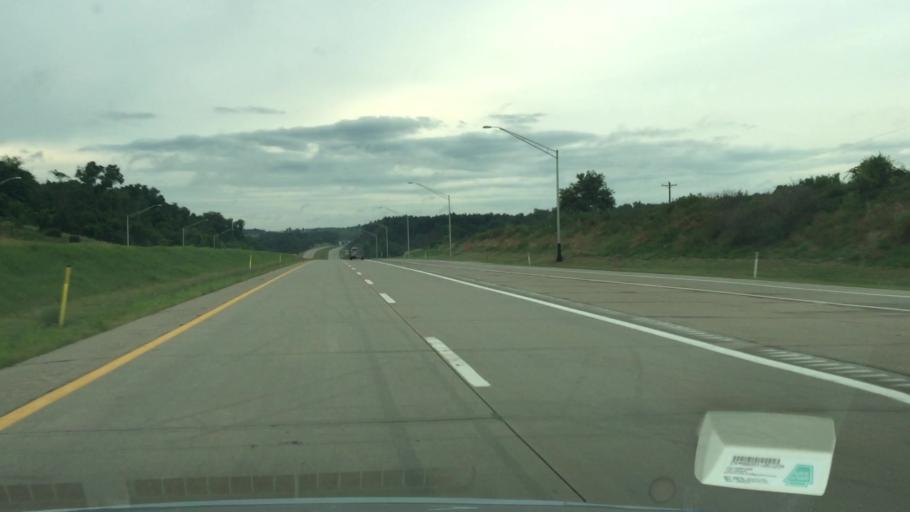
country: US
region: Pennsylvania
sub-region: Allegheny County
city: Imperial
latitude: 40.4708
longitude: -80.2844
